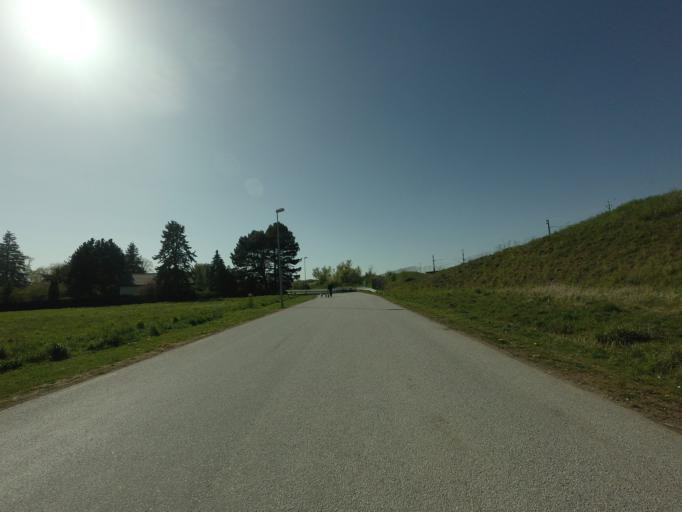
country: SE
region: Skane
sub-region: Landskrona
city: Asmundtorp
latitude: 55.8609
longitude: 12.9094
